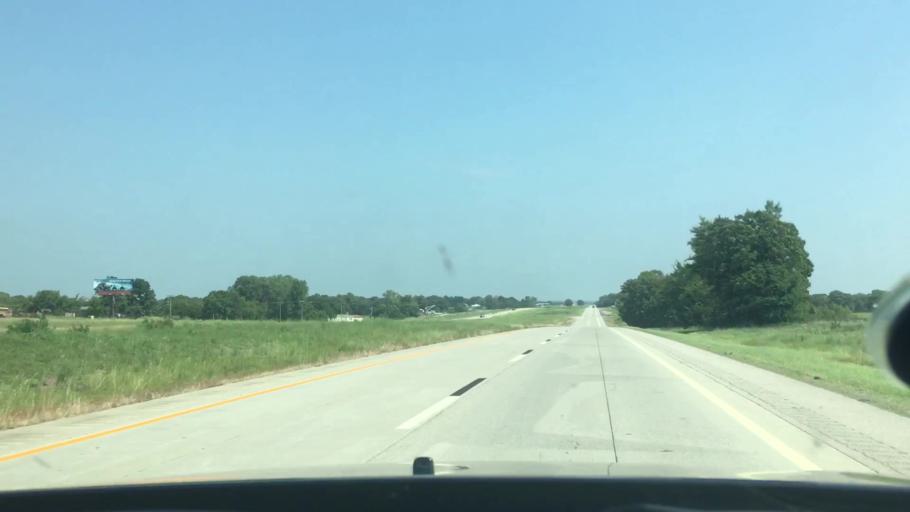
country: US
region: Oklahoma
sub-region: Atoka County
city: Atoka
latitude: 34.1966
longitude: -96.2399
